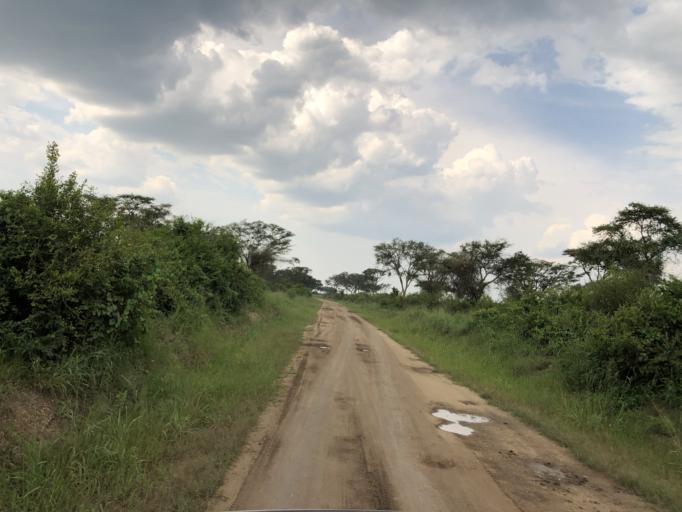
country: UG
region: Western Region
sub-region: Rubirizi District
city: Rubirizi
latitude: -0.2005
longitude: 30.0022
